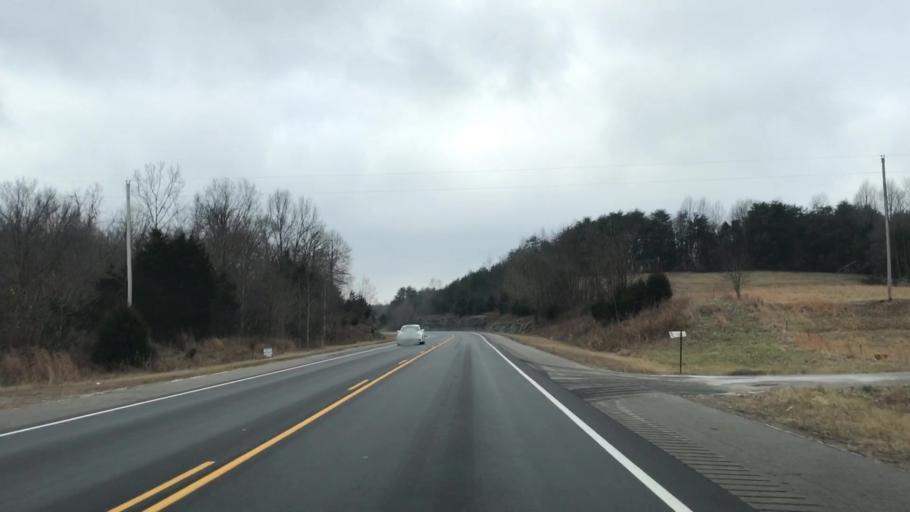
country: US
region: Kentucky
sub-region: Metcalfe County
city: Edmonton
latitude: 36.9524
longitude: -85.4438
